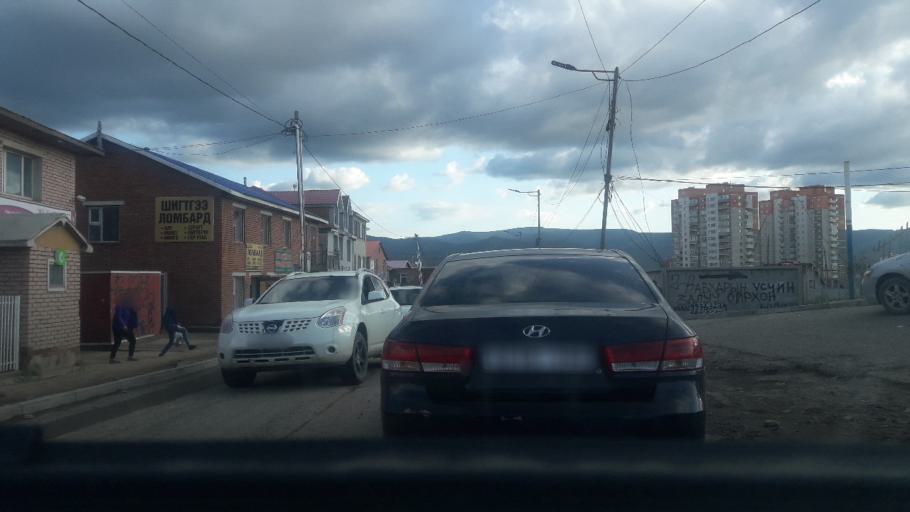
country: MN
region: Ulaanbaatar
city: Ulaanbaatar
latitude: 47.9238
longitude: 106.9963
